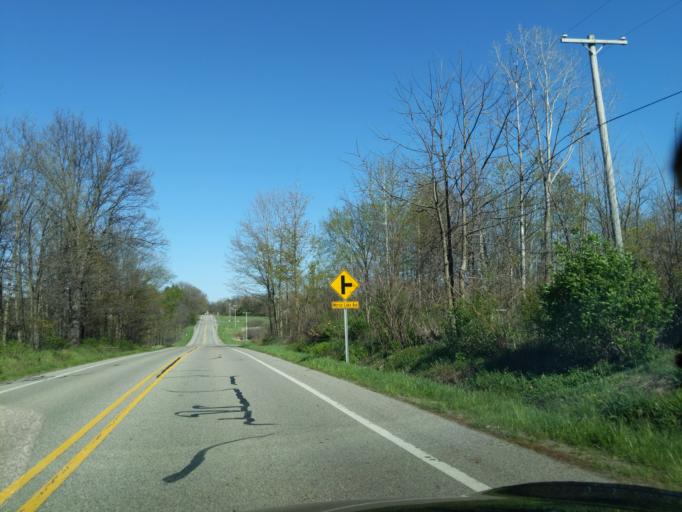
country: US
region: Michigan
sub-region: Kent County
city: Lowell
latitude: 42.8854
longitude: -85.4144
